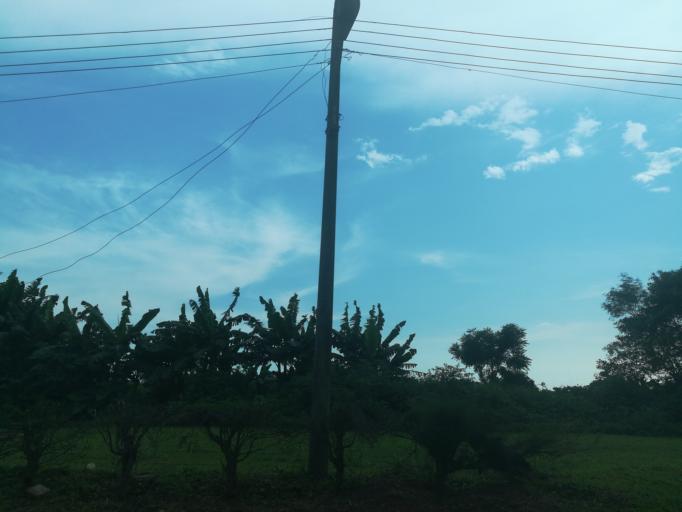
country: NG
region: Lagos
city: Ikorodu
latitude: 6.6455
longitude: 3.5199
